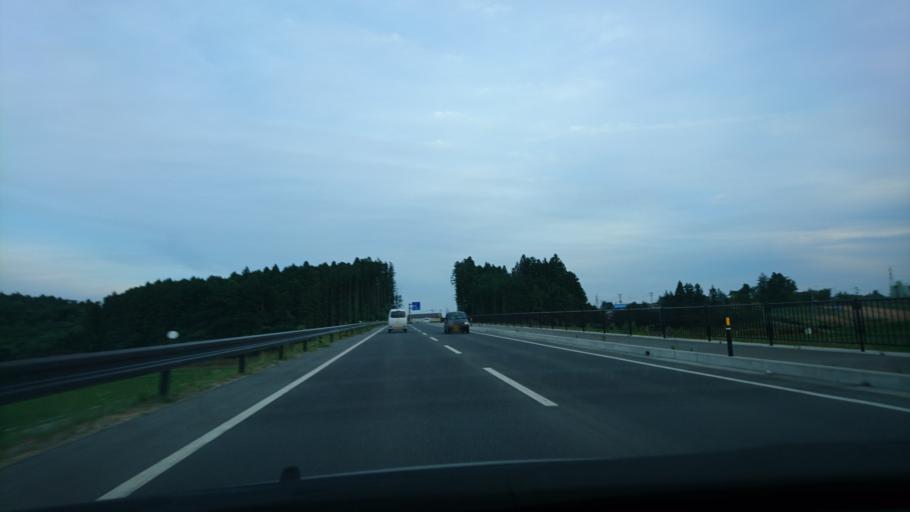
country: JP
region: Miyagi
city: Furukawa
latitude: 38.7455
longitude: 141.0371
